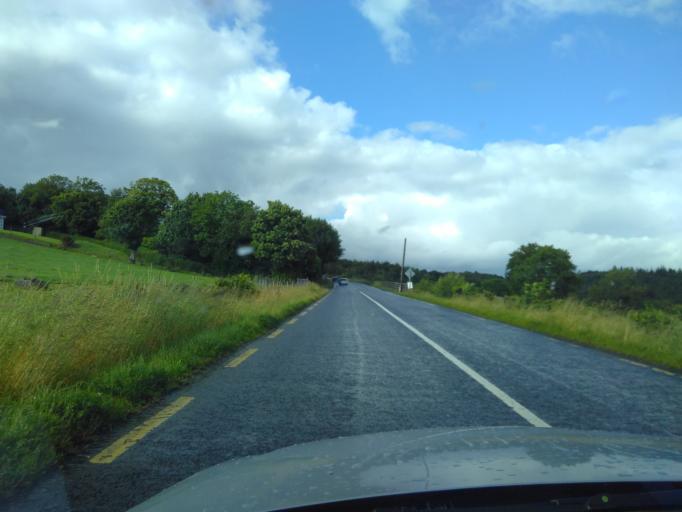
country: IE
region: Ulster
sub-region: County Donegal
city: Letterkenny
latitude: 54.9674
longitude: -7.6900
